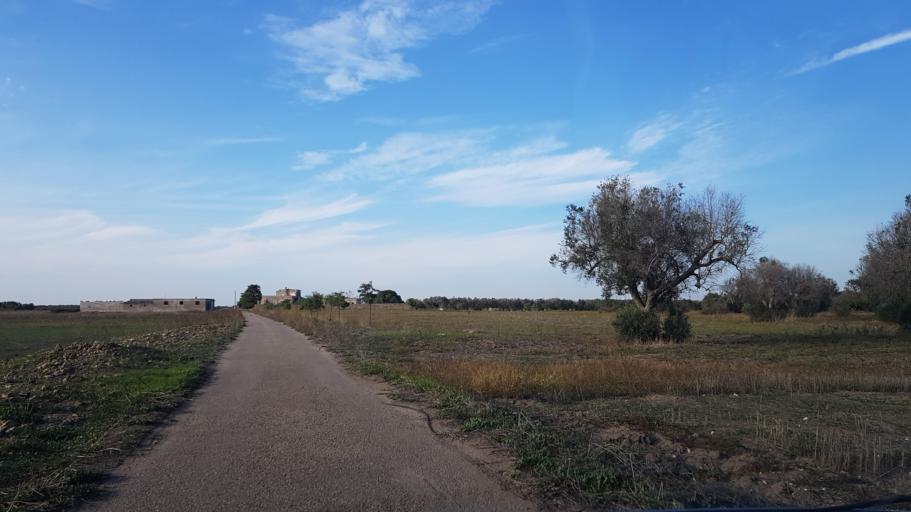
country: IT
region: Apulia
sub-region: Provincia di Brindisi
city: San Pancrazio Salentino
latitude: 40.4942
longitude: 17.8536
